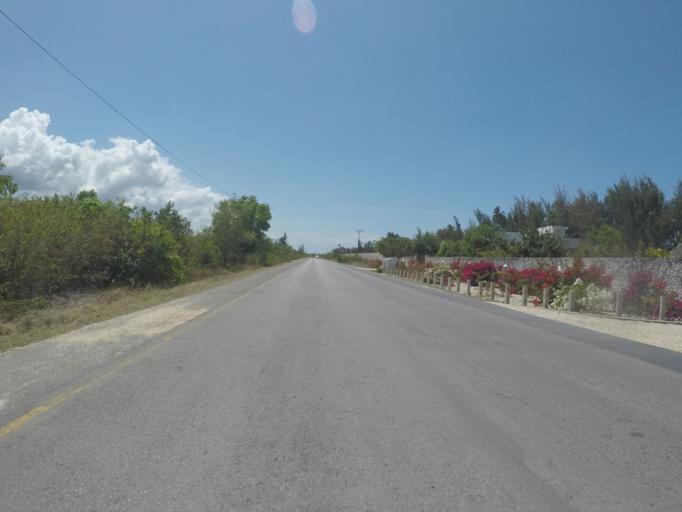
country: TZ
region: Zanzibar Central/South
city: Nganane
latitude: -6.2801
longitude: 39.5350
